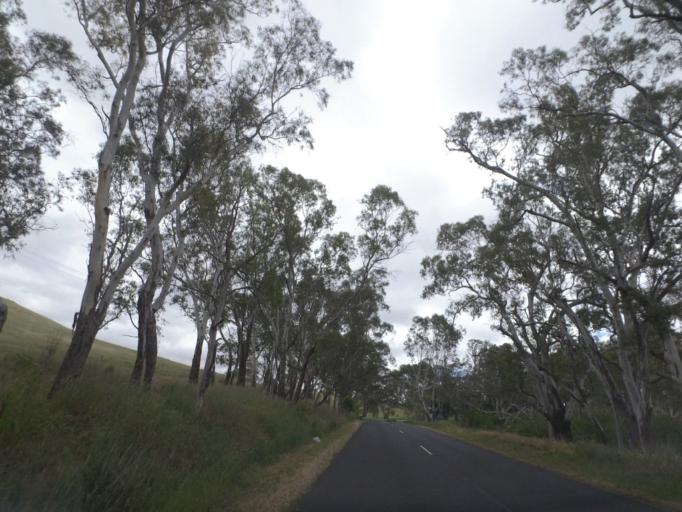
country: AU
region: Victoria
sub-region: Whittlesea
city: Whittlesea
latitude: -37.1919
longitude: 145.0385
